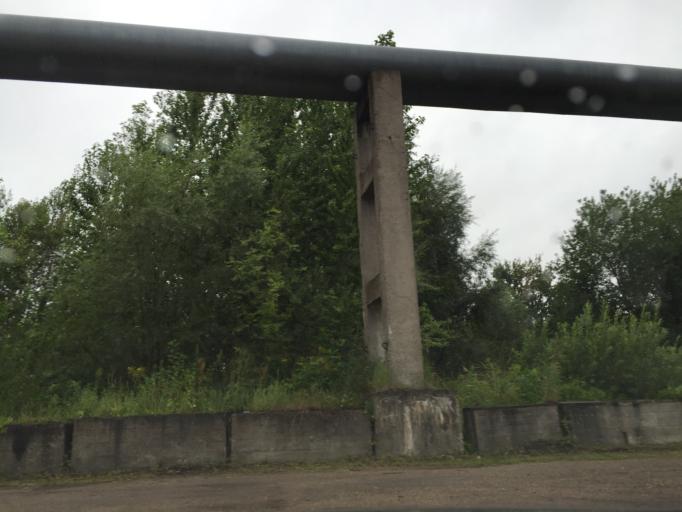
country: LV
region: Riga
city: Riga
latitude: 56.9840
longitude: 24.1130
